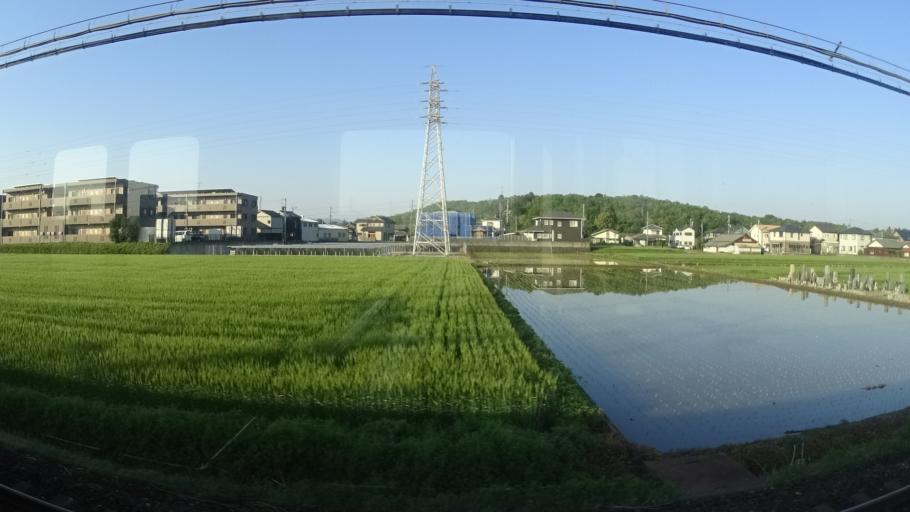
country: JP
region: Mie
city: Ise
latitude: 34.5242
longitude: 136.6617
